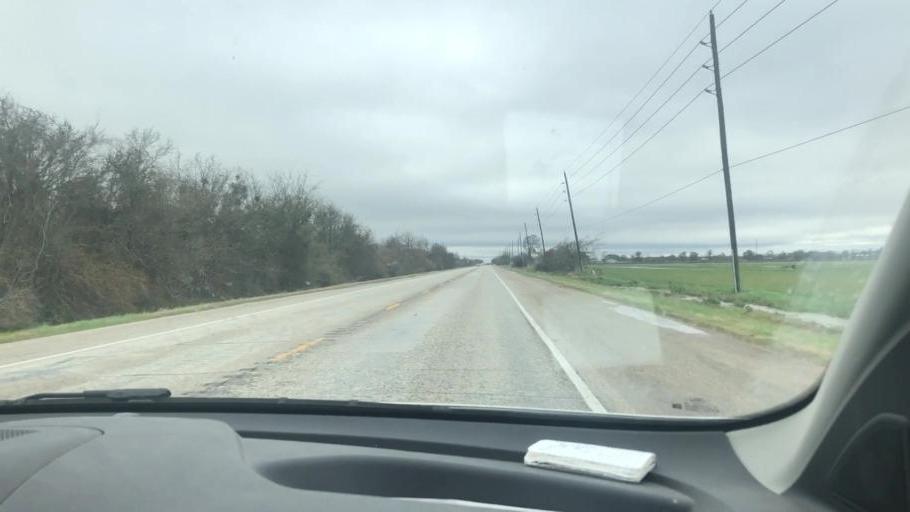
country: US
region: Texas
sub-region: Wharton County
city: Wharton
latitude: 29.2752
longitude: -96.0630
